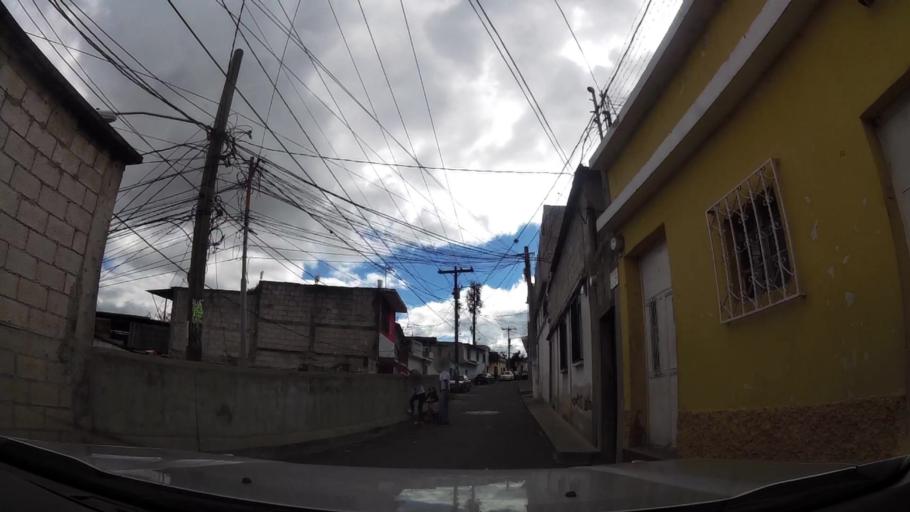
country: GT
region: Guatemala
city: Mixco
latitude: 14.6308
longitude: -90.5995
